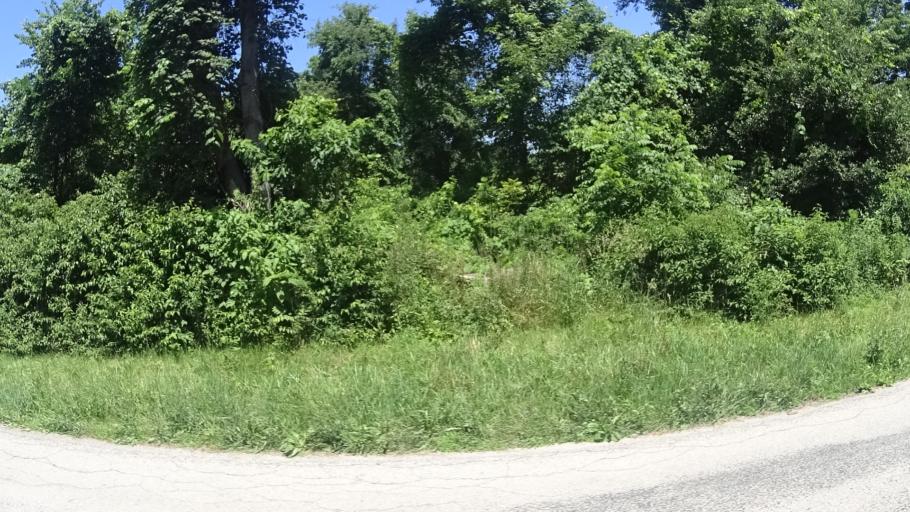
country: US
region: Ohio
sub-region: Lorain County
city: Vermilion
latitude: 41.3394
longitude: -82.3757
